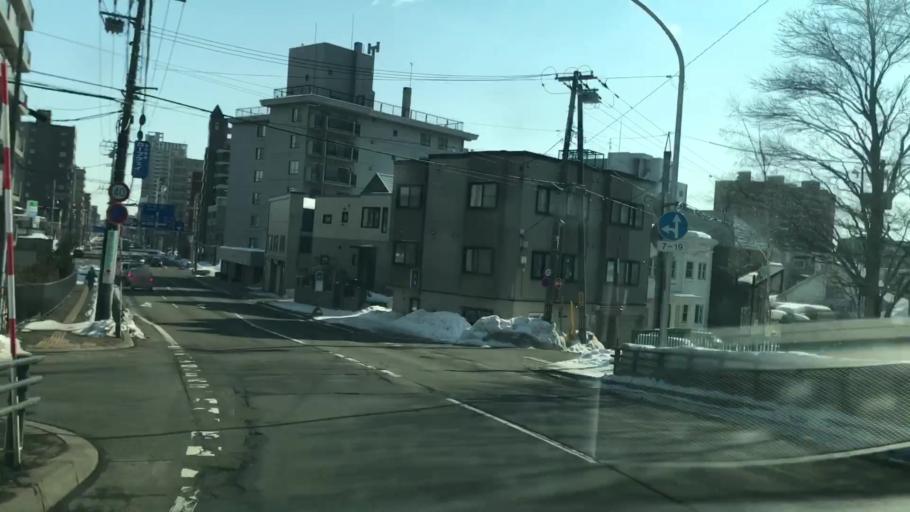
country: JP
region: Hokkaido
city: Sapporo
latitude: 43.0333
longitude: 141.3333
